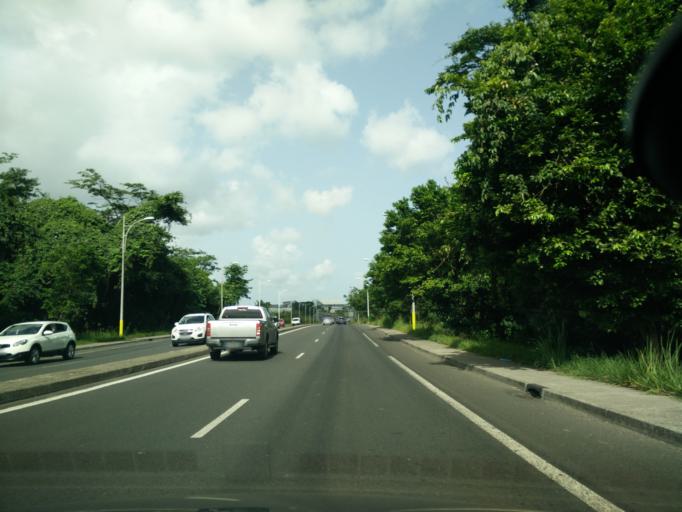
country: GP
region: Guadeloupe
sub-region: Guadeloupe
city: Baie-Mahault
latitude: 16.2401
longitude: -61.5792
